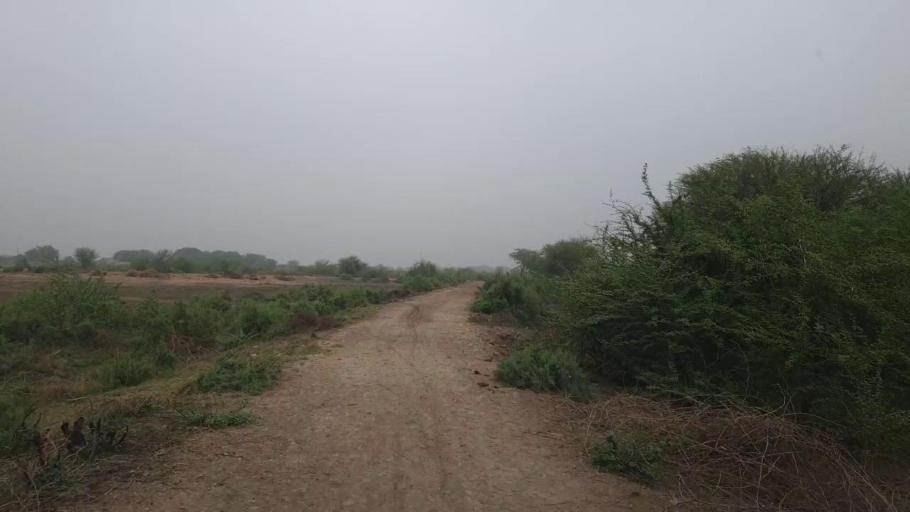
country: PK
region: Sindh
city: Badin
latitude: 24.6011
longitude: 68.6695
